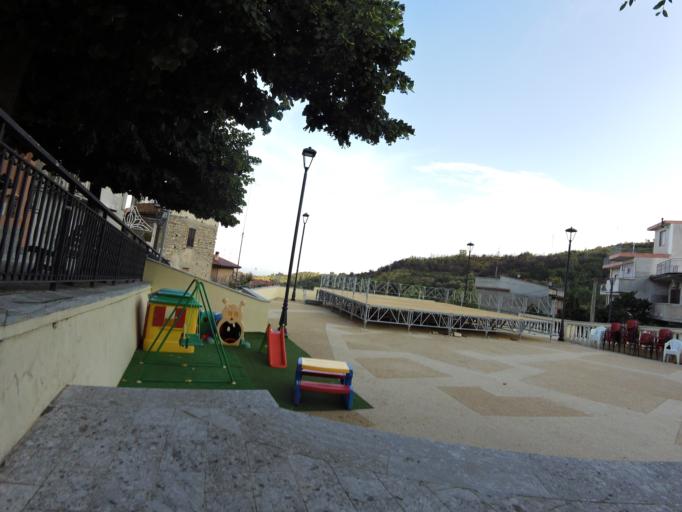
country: IT
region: Calabria
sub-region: Provincia di Reggio Calabria
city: Camini
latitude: 38.4321
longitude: 16.4818
